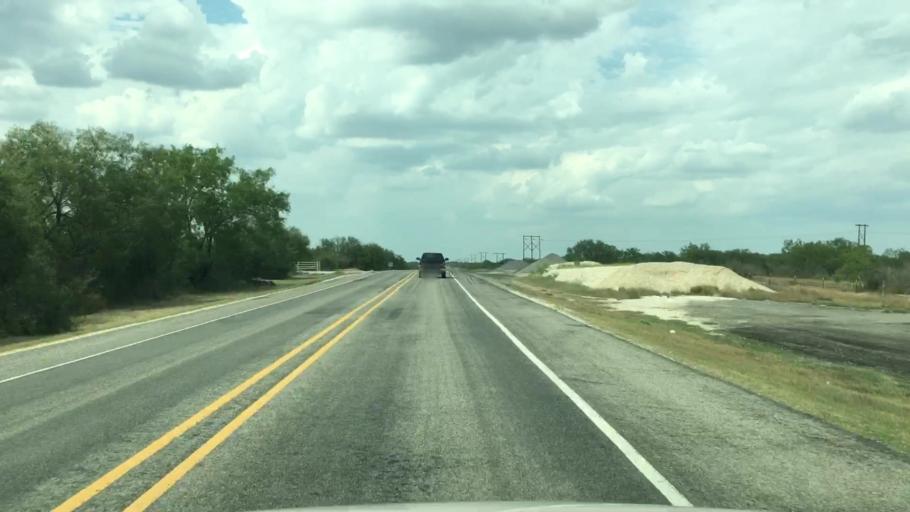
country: US
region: Texas
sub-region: Live Oak County
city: Three Rivers
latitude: 28.6461
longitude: -98.2846
